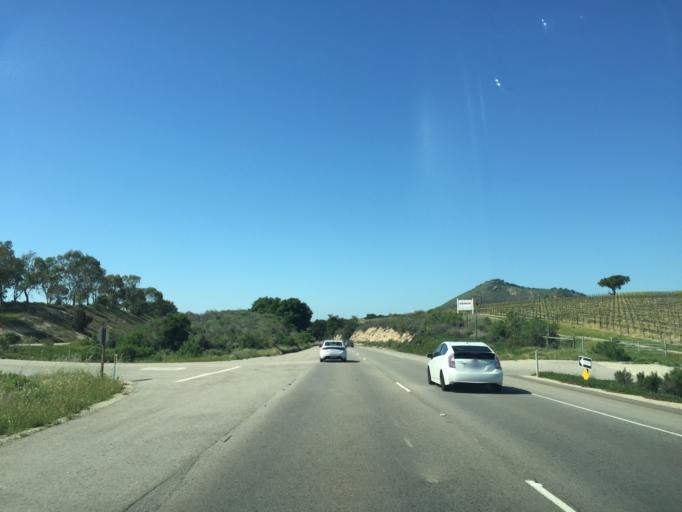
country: US
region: California
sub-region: San Luis Obispo County
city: Nipomo
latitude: 35.0839
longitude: -120.5298
